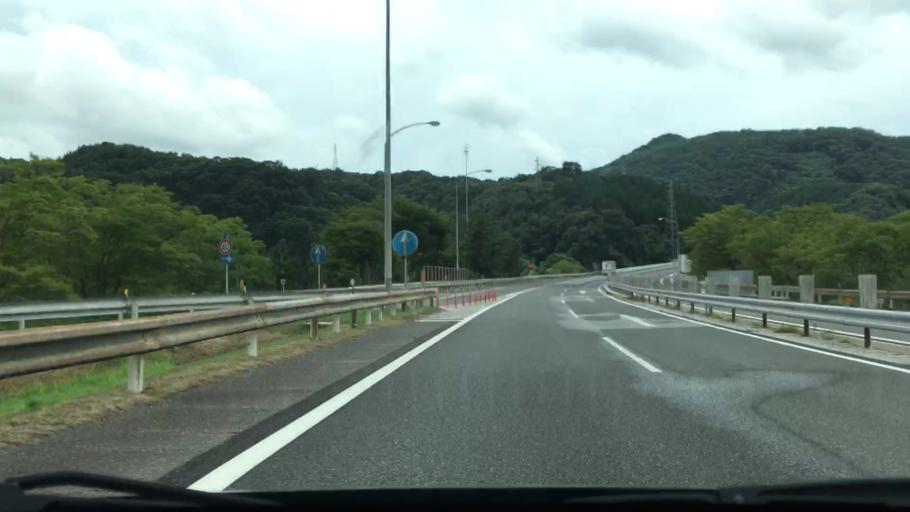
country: JP
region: Okayama
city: Niimi
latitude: 34.8884
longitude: 133.2797
